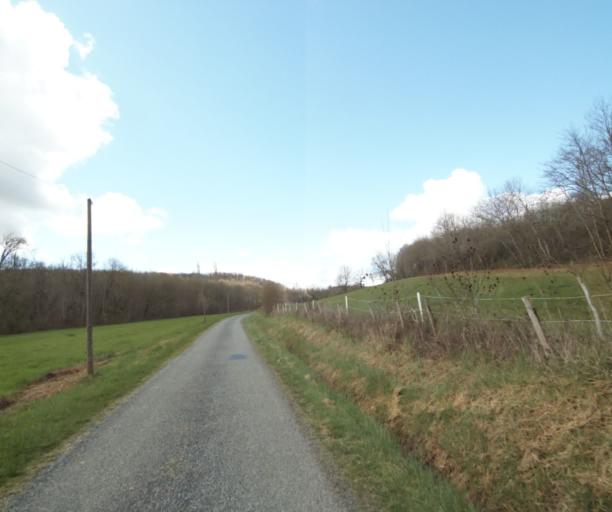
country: FR
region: Midi-Pyrenees
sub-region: Departement de l'Ariege
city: Saverdun
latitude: 43.1855
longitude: 1.5580
